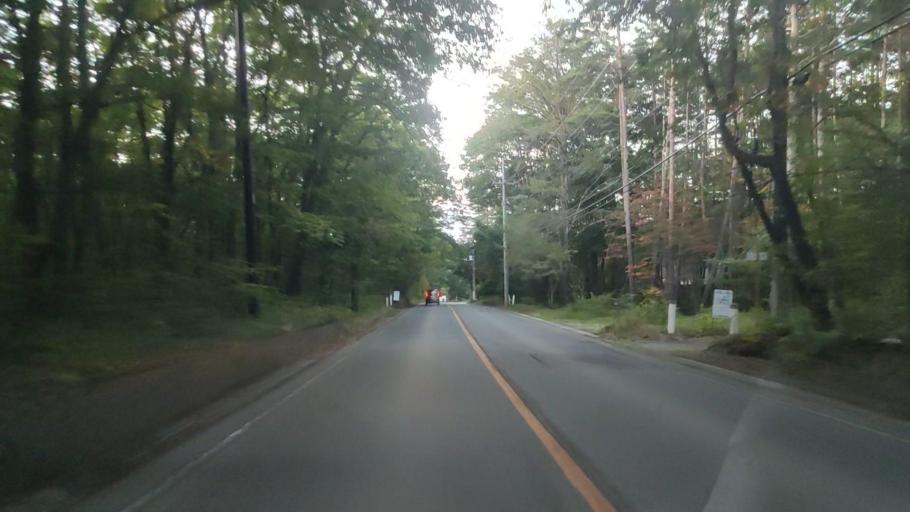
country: JP
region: Nagano
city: Komoro
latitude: 36.4455
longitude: 138.5797
